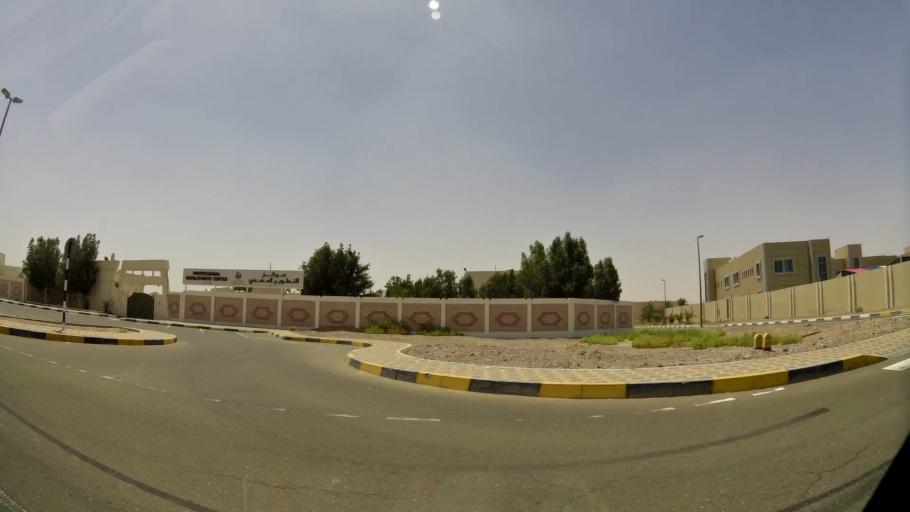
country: AE
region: Abu Dhabi
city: Al Ain
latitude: 24.2597
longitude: 55.7038
